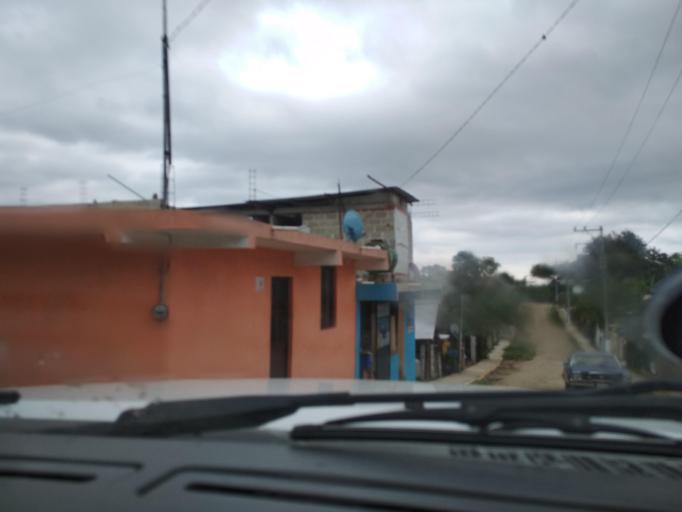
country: MX
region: Veracruz
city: El Castillo
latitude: 19.5726
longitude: -96.8498
